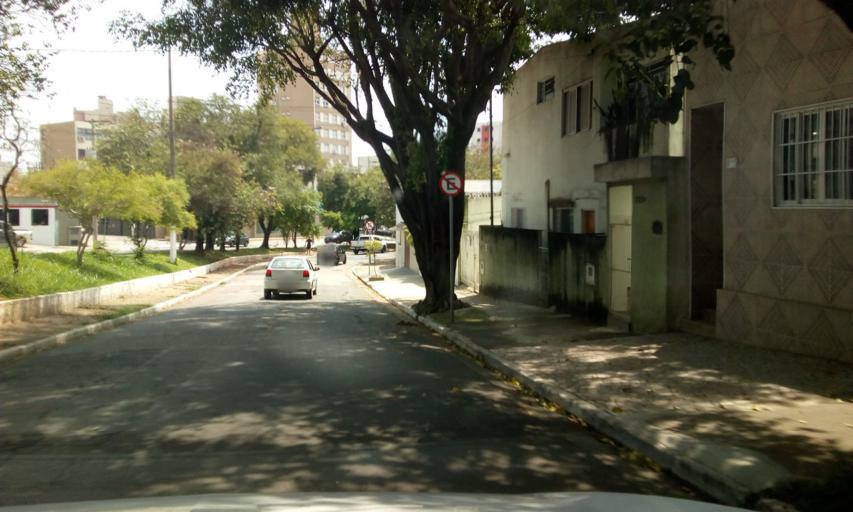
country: BR
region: Sao Paulo
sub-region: Jundiai
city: Jundiai
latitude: -23.2031
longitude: -46.8849
